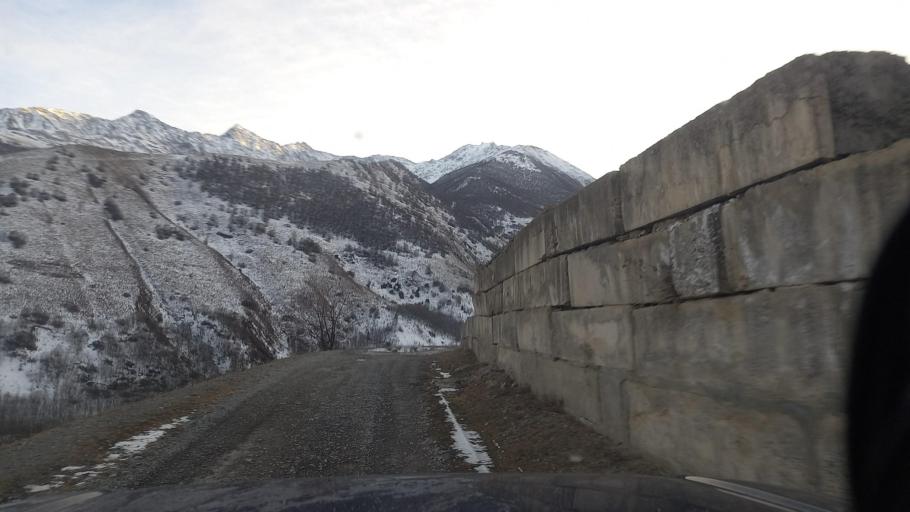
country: RU
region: Ingushetiya
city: Dzhayrakh
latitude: 42.8415
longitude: 44.5125
